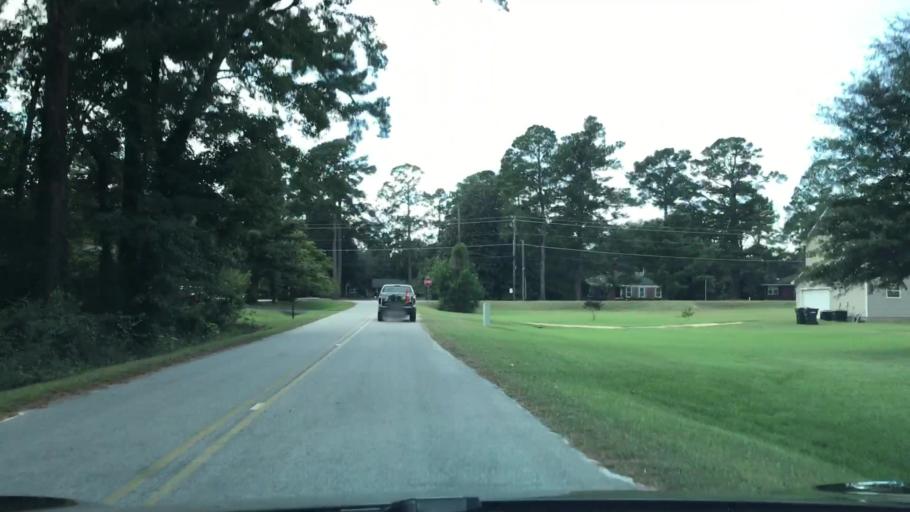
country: US
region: Georgia
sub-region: Jefferson County
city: Wadley
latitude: 32.8713
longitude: -82.4031
